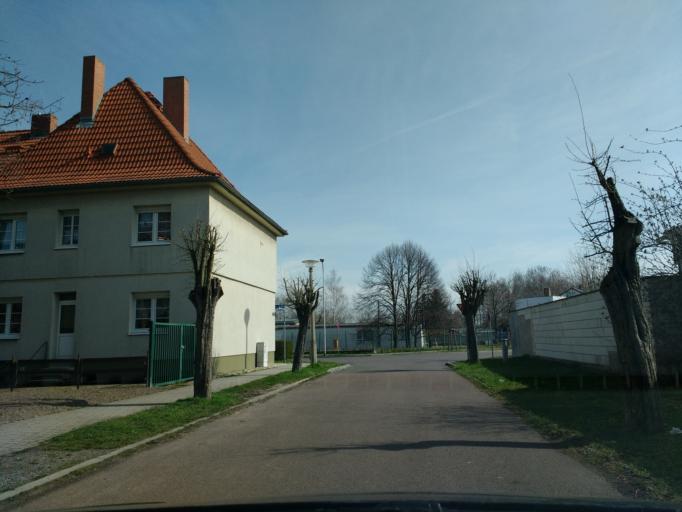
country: DE
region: Saxony-Anhalt
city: Halle (Saale)
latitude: 51.4889
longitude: 12.0084
